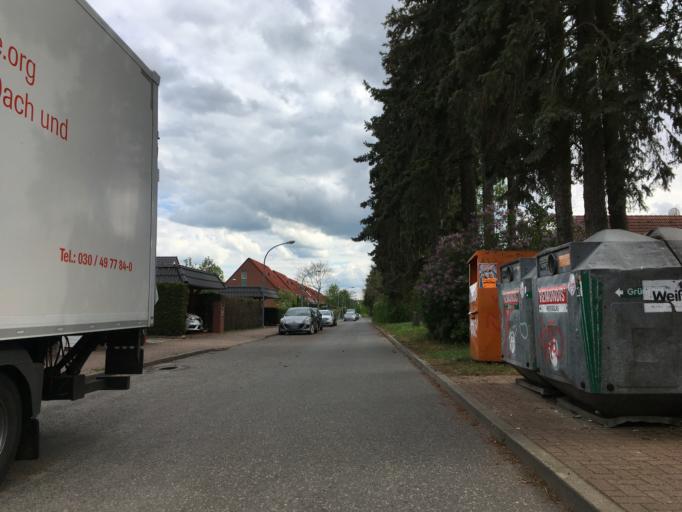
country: DE
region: Brandenburg
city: Bernau bei Berlin
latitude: 52.6997
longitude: 13.5944
